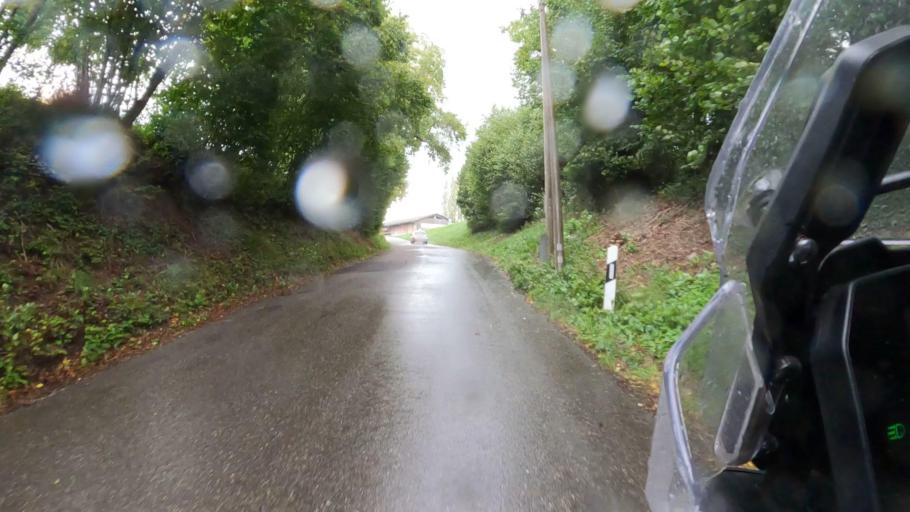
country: CH
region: Schaffhausen
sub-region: Bezirk Unterklettgau
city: Wilchingen
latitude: 47.6637
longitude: 8.4679
